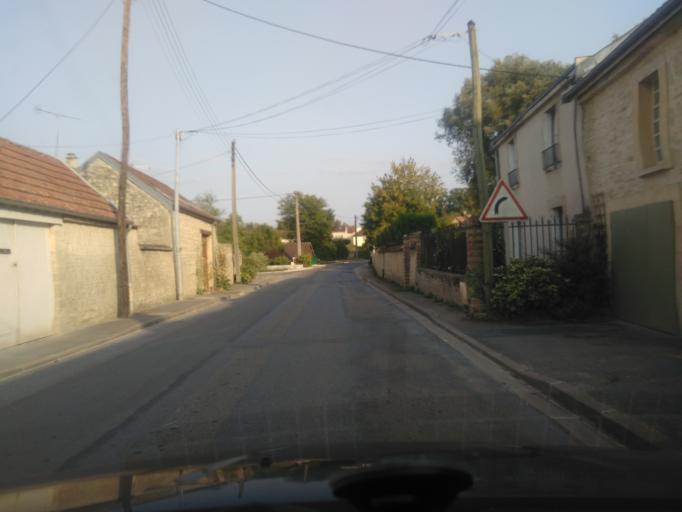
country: FR
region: Champagne-Ardenne
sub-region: Departement de la Marne
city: Fismes
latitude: 49.2676
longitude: 3.6976
